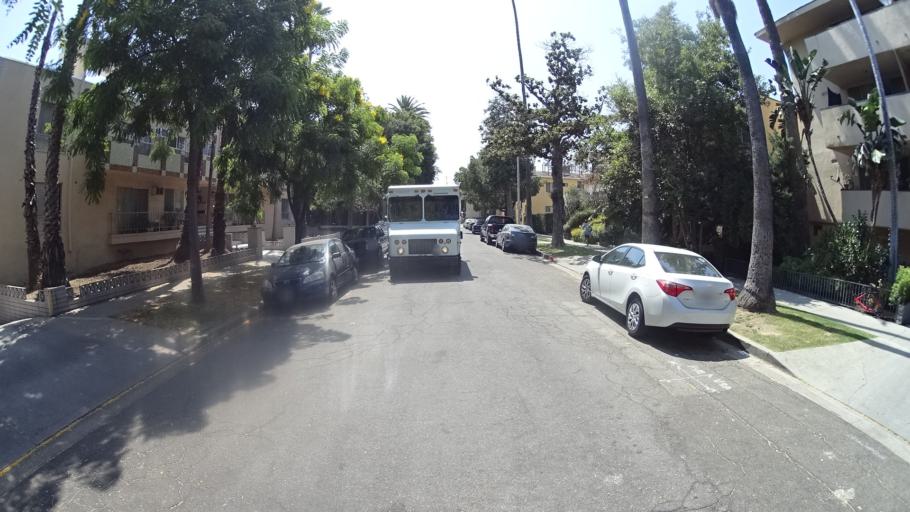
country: US
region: California
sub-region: Los Angeles County
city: West Hollywood
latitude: 34.0935
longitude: -118.3572
